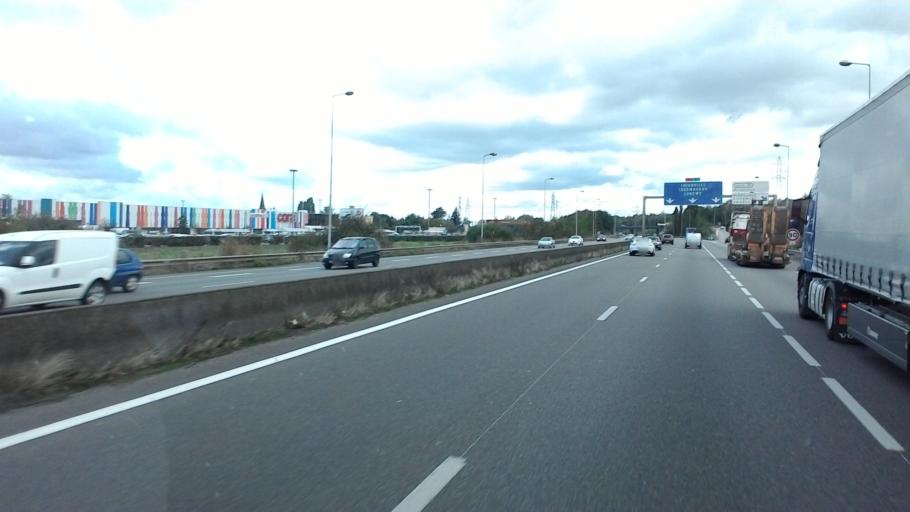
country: FR
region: Lorraine
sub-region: Departement de la Moselle
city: Mondelange
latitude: 49.2580
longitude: 6.1772
